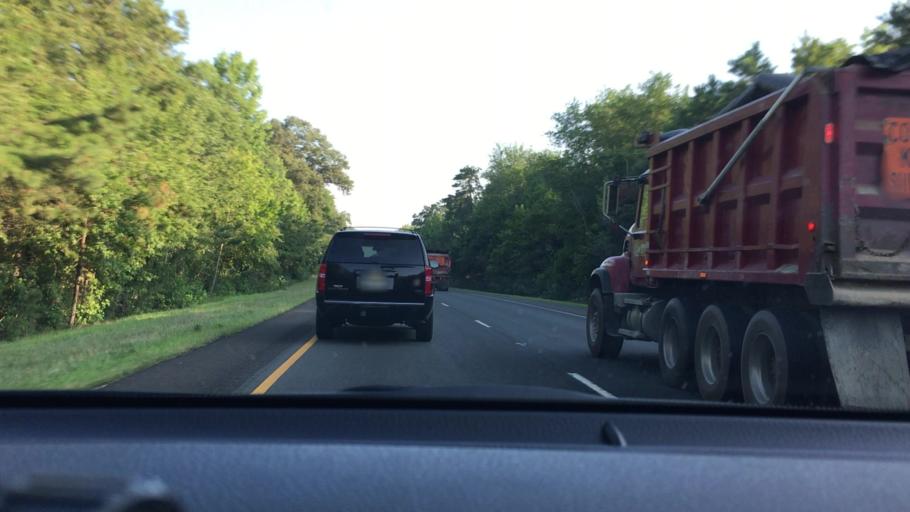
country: US
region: New Jersey
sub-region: Gloucester County
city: Clayton
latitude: 39.6302
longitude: -75.0925
